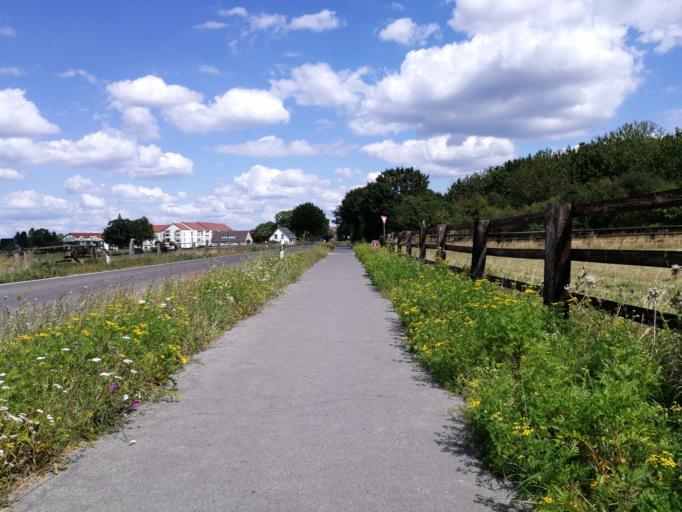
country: DE
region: North Rhine-Westphalia
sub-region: Regierungsbezirk Dusseldorf
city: Dormagen
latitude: 51.1091
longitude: 6.7708
